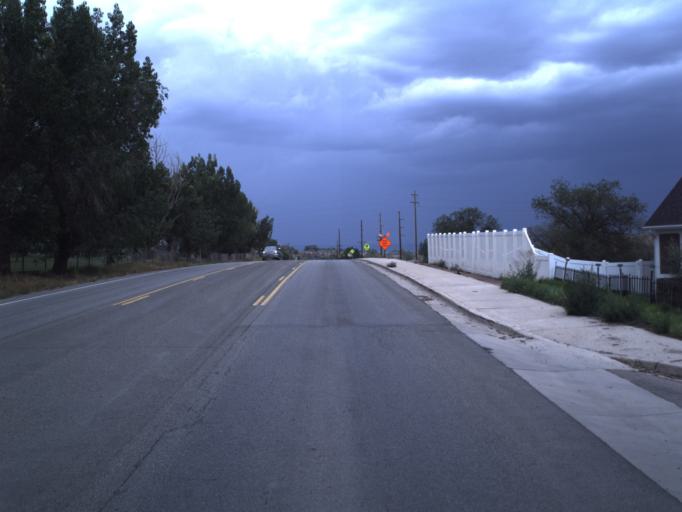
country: US
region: Utah
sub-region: Duchesne County
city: Roosevelt
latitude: 40.3055
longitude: -110.0033
